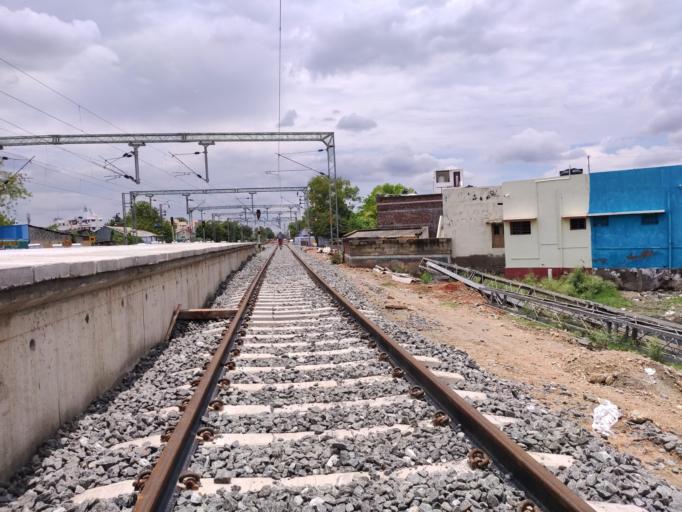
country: IN
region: Tamil Nadu
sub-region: Thoothukkudi
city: Kovilpatti
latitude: 9.1802
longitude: 77.8695
